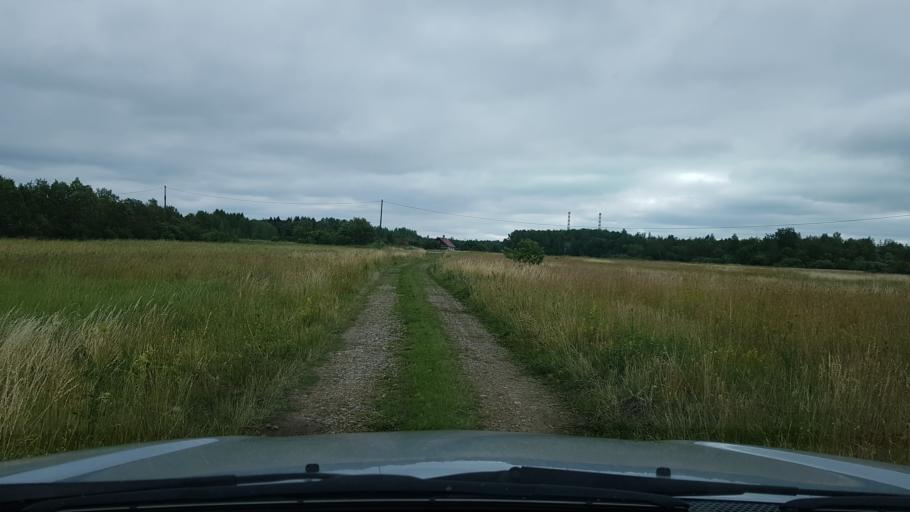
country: EE
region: Ida-Virumaa
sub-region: Narva linn
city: Narva
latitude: 59.3793
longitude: 28.1209
